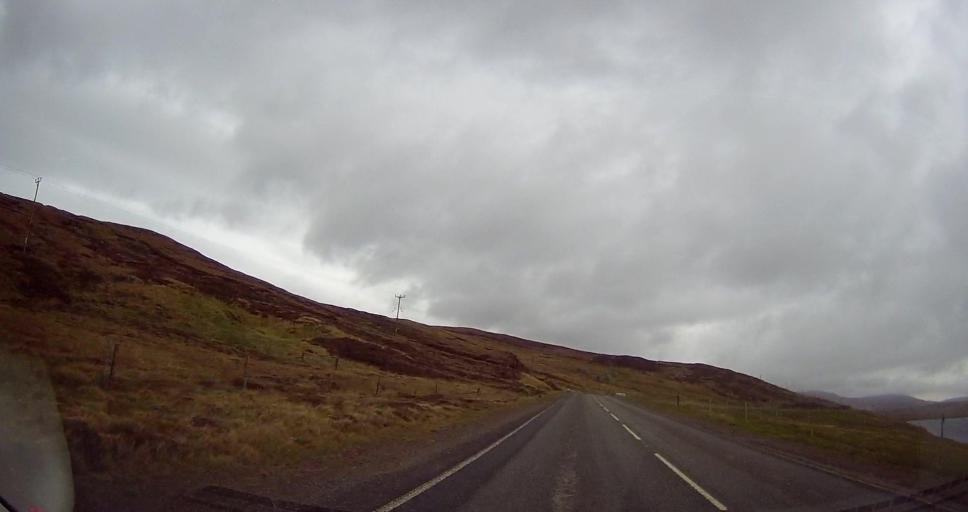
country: GB
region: Scotland
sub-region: Shetland Islands
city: Lerwick
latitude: 60.2528
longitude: -1.2259
